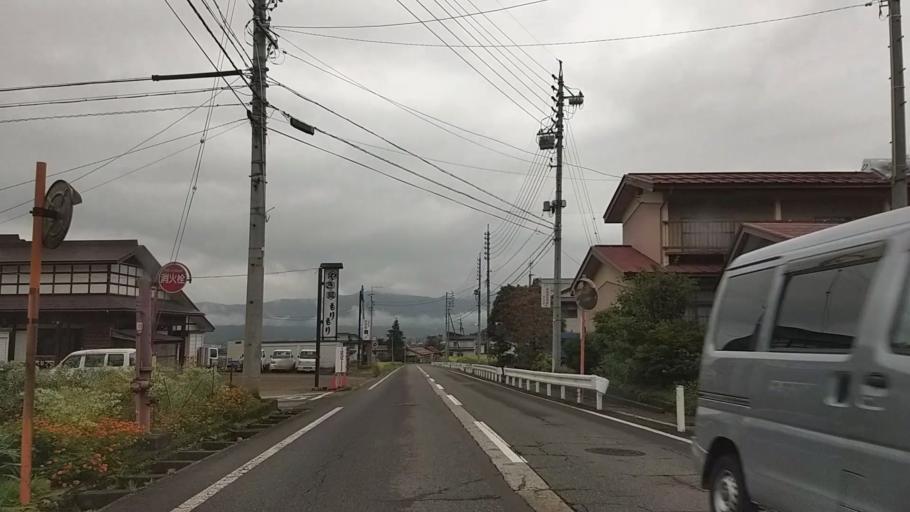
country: JP
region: Nagano
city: Iiyama
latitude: 36.8404
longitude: 138.4072
